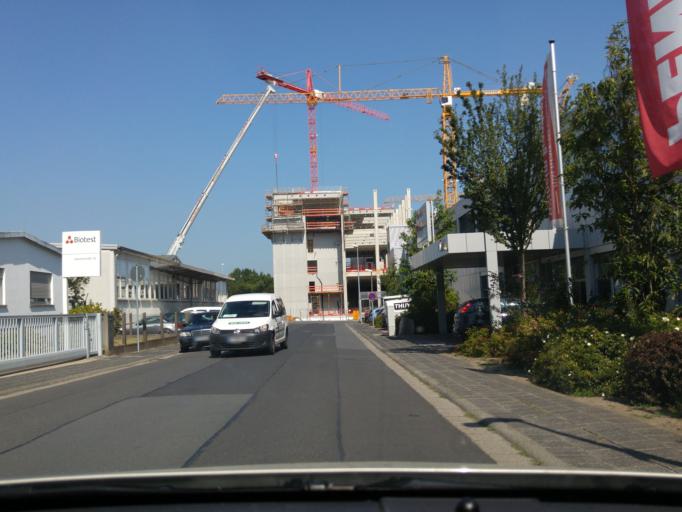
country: DE
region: Hesse
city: Dreieich
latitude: 50.0053
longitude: 8.7012
